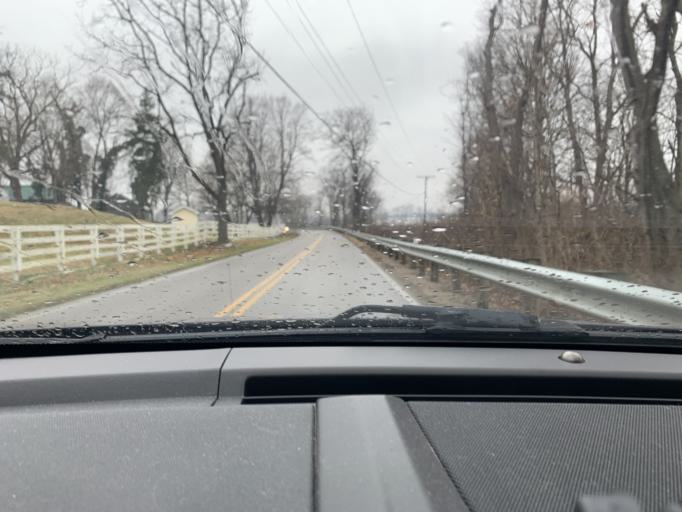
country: US
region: Ohio
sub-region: Ross County
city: Chillicothe
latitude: 39.3848
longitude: -82.9563
